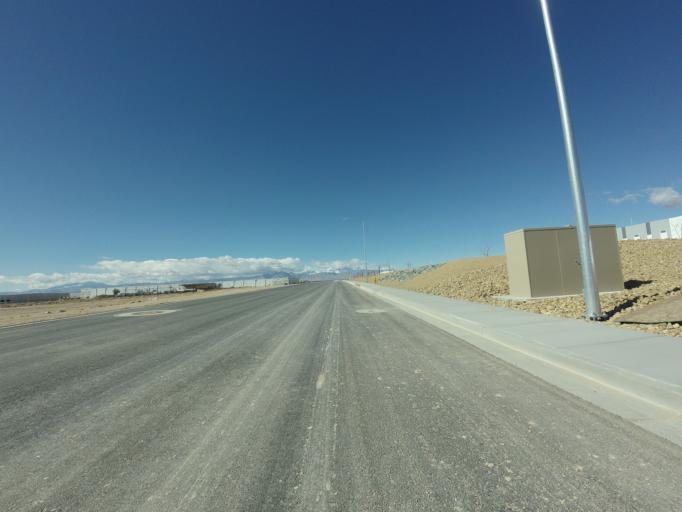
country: US
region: Nevada
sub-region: Clark County
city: Nellis Air Force Base
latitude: 36.2623
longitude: -115.0394
